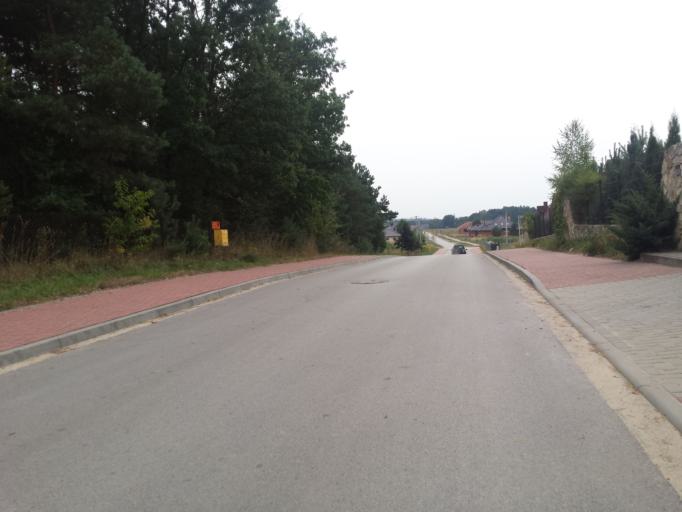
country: PL
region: Swietokrzyskie
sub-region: Powiat kielecki
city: Morawica
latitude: 50.7650
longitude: 20.6323
